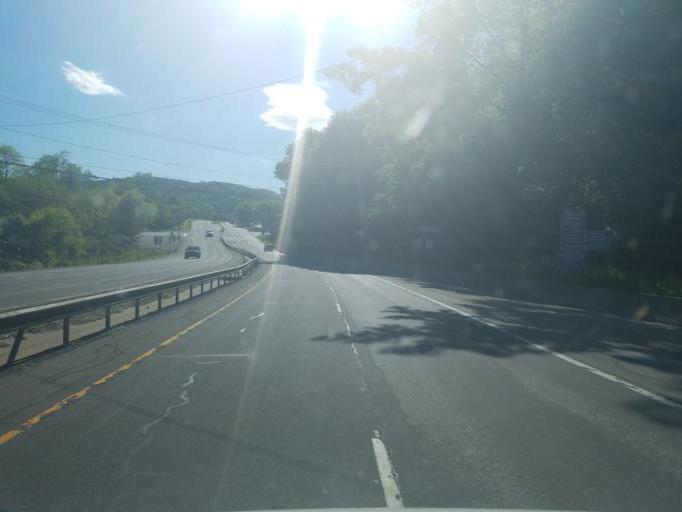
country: US
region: New York
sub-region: Herkimer County
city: Little Falls
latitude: 43.0429
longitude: -74.8480
